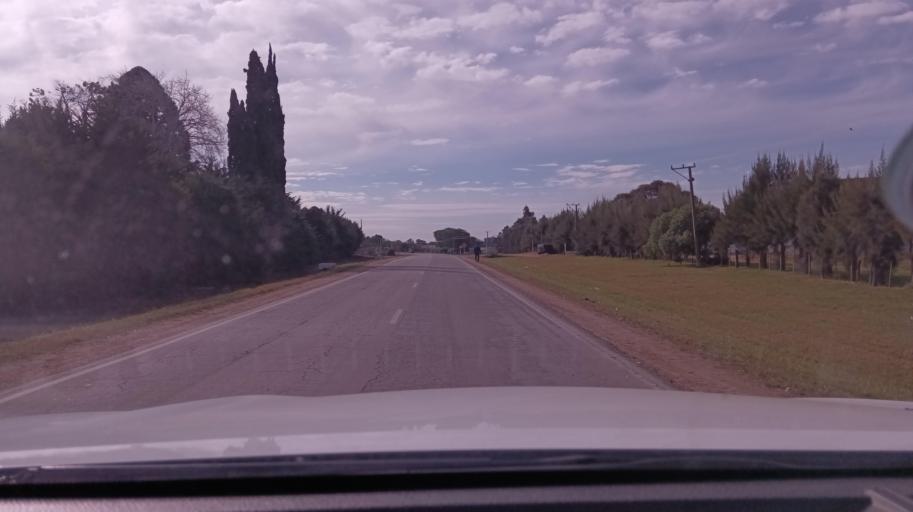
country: UY
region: Canelones
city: Toledo
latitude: -34.7304
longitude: -56.1137
